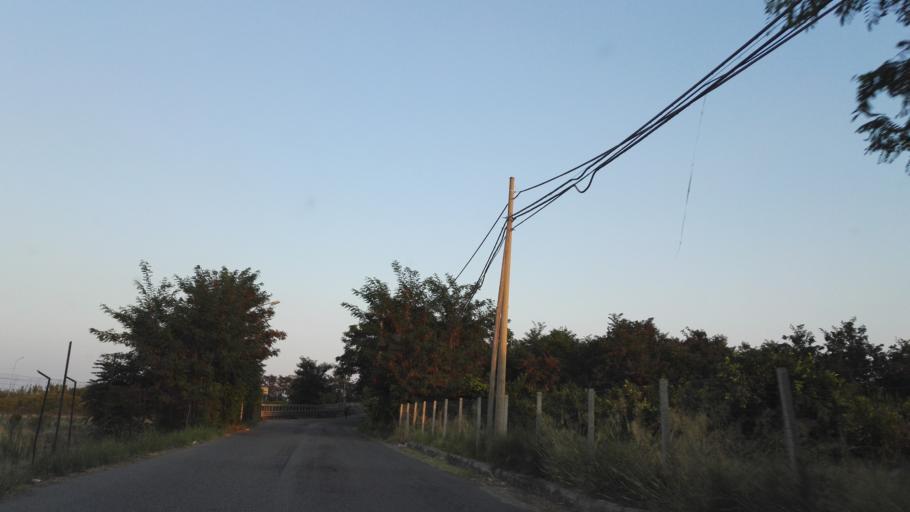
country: IT
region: Calabria
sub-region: Provincia di Reggio Calabria
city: Caulonia Marina
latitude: 38.3508
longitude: 16.4738
